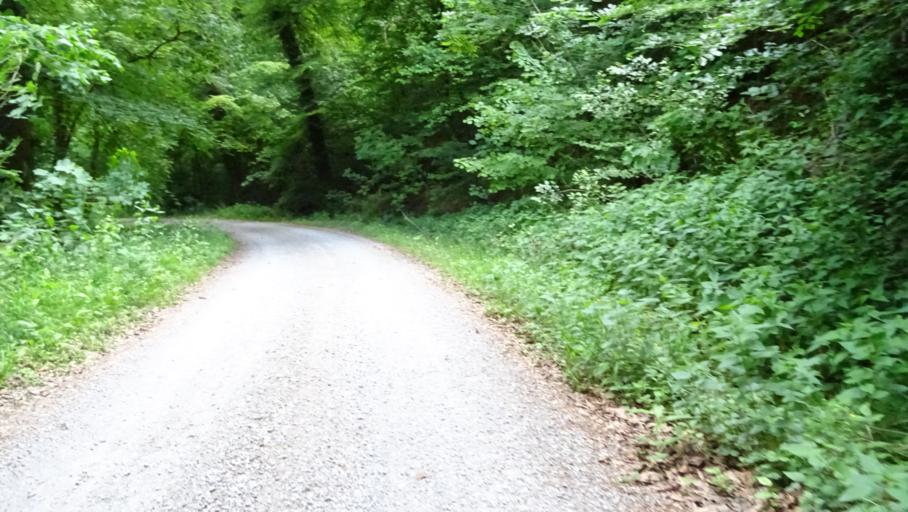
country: DE
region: Baden-Wuerttemberg
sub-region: Karlsruhe Region
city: Hassmersheim
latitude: 49.3005
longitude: 9.1583
